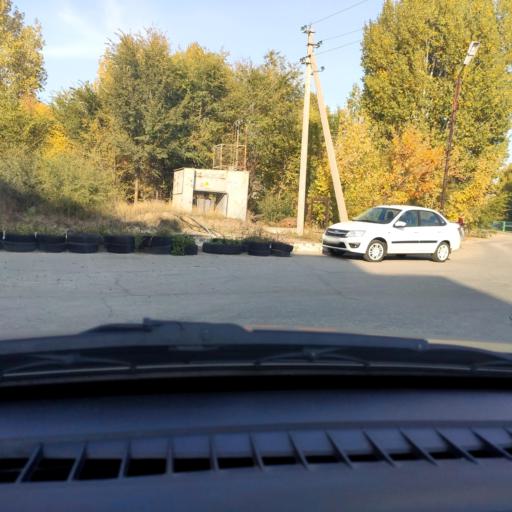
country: RU
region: Samara
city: Tol'yatti
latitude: 53.5365
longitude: 49.3039
